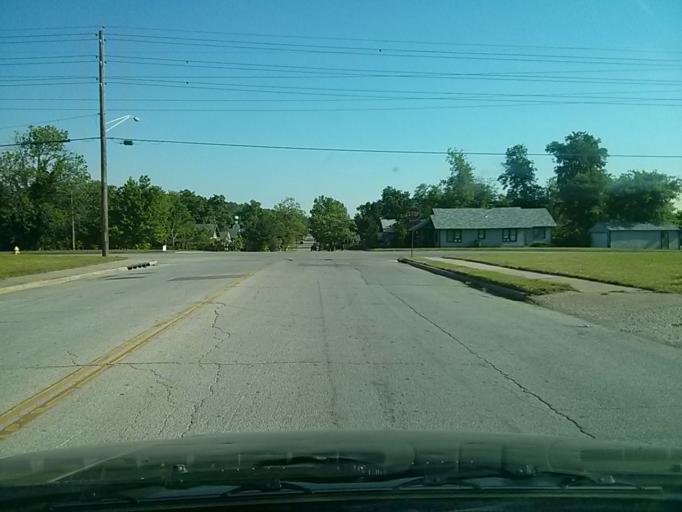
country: US
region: Oklahoma
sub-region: Tulsa County
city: Tulsa
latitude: 36.1765
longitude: -95.9968
